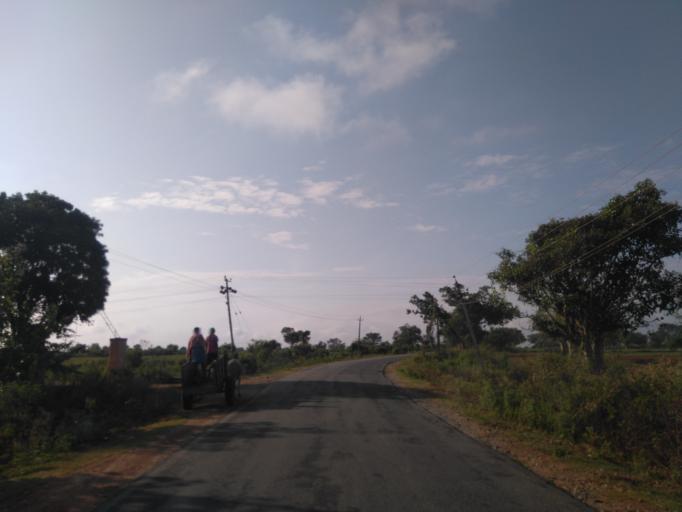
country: IN
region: Karnataka
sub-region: Mandya
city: Malavalli
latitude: 12.3106
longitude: 77.0721
